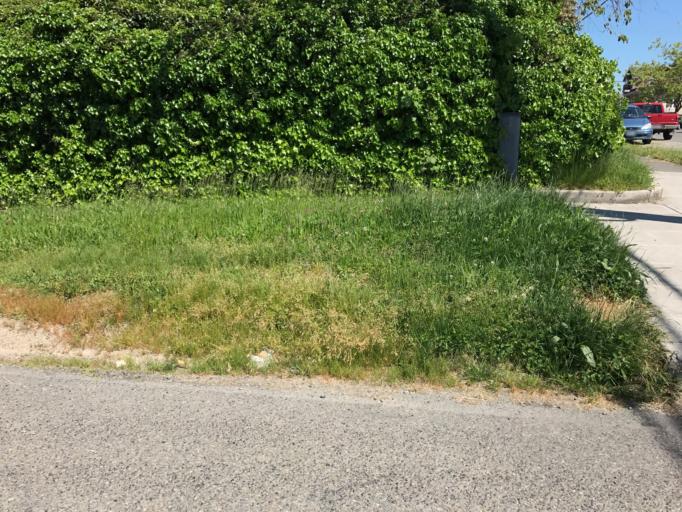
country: US
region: Washington
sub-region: King County
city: Seattle
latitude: 47.5855
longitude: -122.3005
